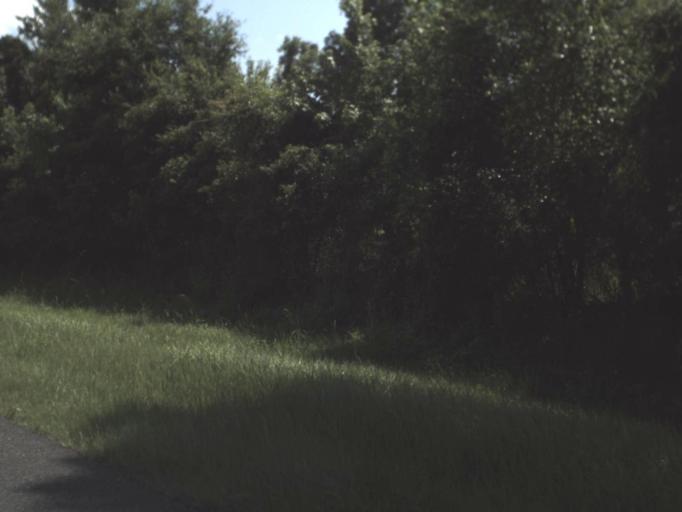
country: US
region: Florida
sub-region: Alachua County
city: Waldo
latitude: 29.7194
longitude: -82.1406
